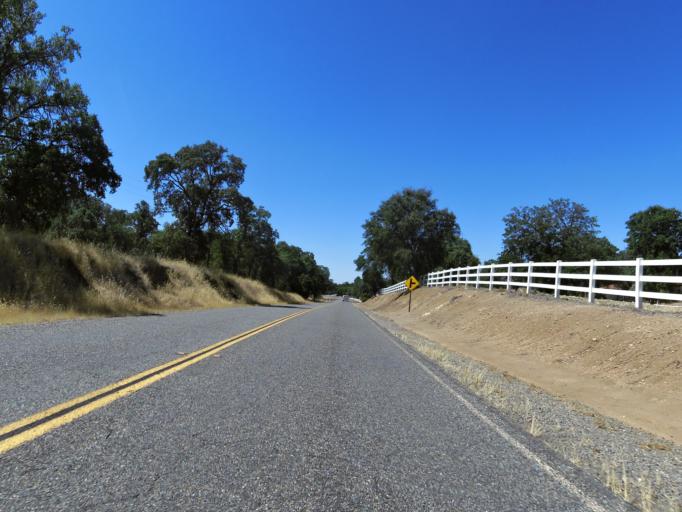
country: US
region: California
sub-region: Mariposa County
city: Mariposa
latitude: 37.4681
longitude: -120.1051
